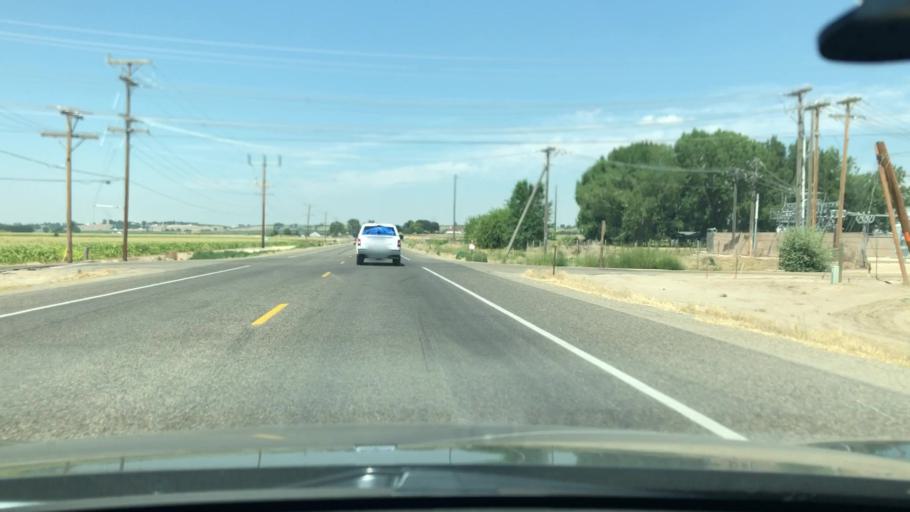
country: US
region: Idaho
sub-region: Owyhee County
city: Homedale
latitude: 43.6320
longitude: -116.9120
